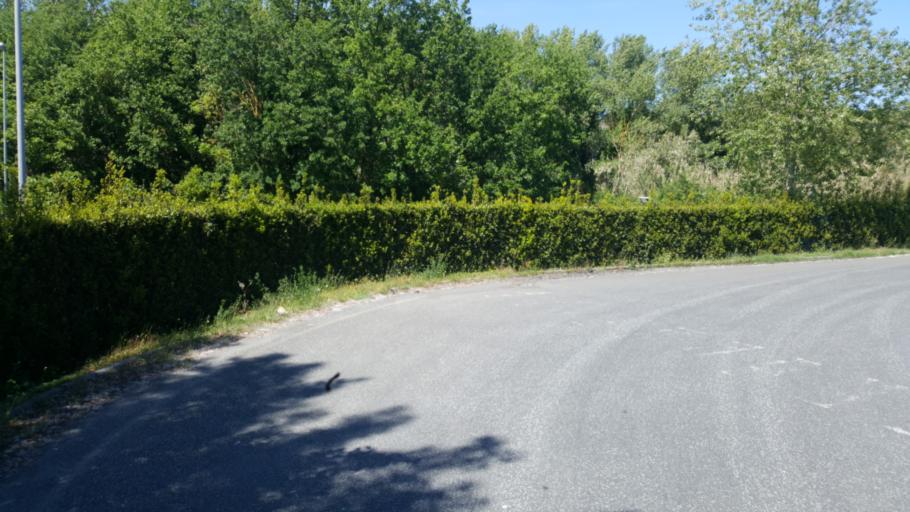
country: IT
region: Tuscany
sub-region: Province of Pisa
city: Castellina Marittima
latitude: 43.4213
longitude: 10.5429
